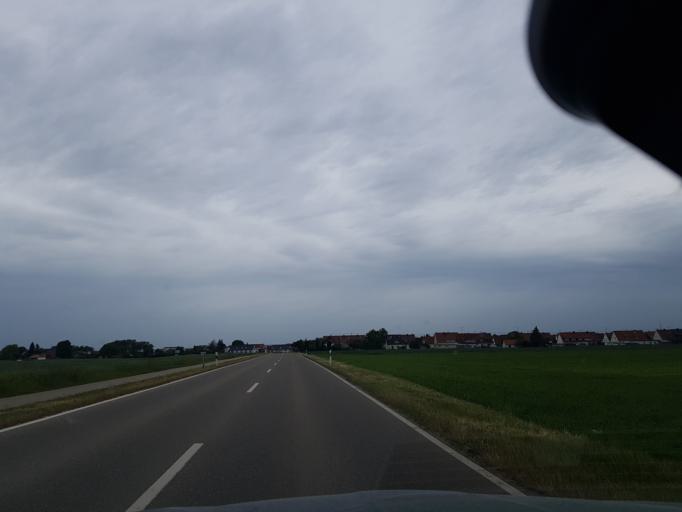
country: DE
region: Bavaria
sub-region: Swabia
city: Nersingen
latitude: 48.4253
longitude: 10.1675
